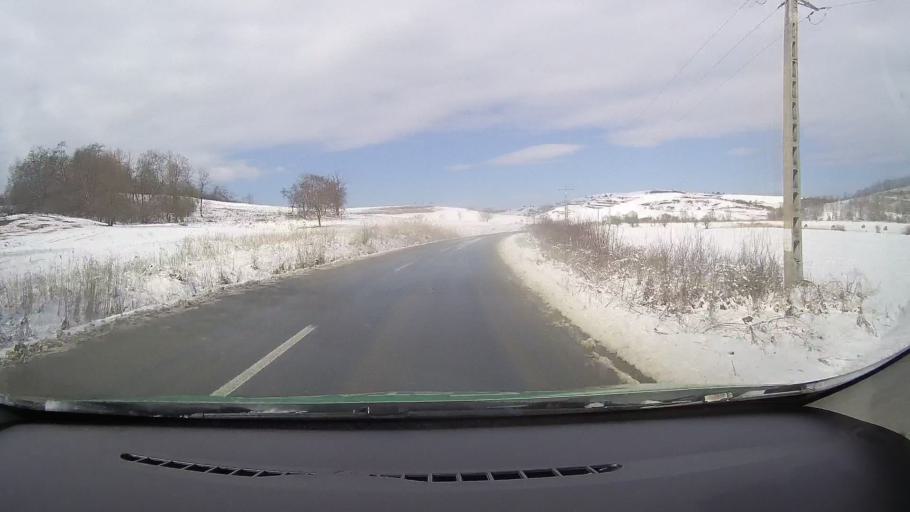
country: RO
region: Sibiu
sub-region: Comuna Altina
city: Altina
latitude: 45.9707
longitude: 24.4672
